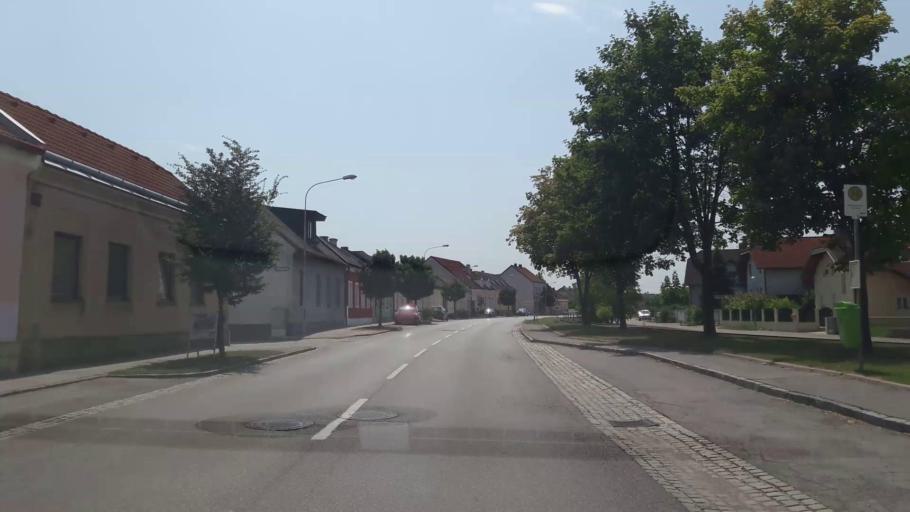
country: AT
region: Lower Austria
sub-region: Politischer Bezirk Wien-Umgebung
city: Schwadorf
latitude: 48.0425
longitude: 16.6040
